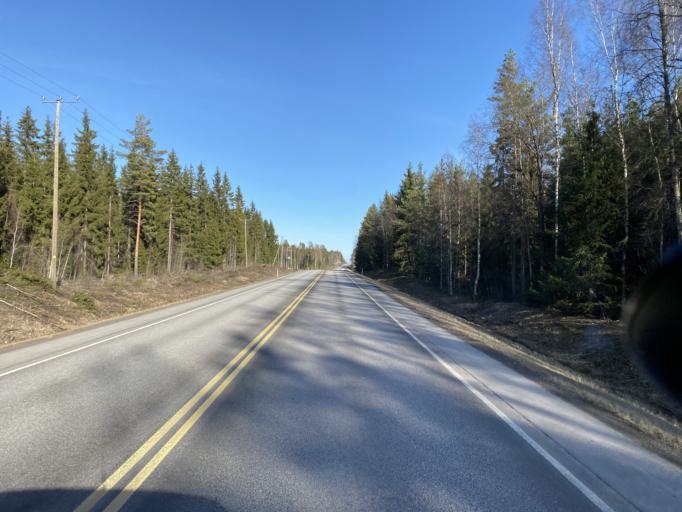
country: FI
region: Satakunta
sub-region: Rauma
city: Kiukainen
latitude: 61.1312
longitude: 22.0150
